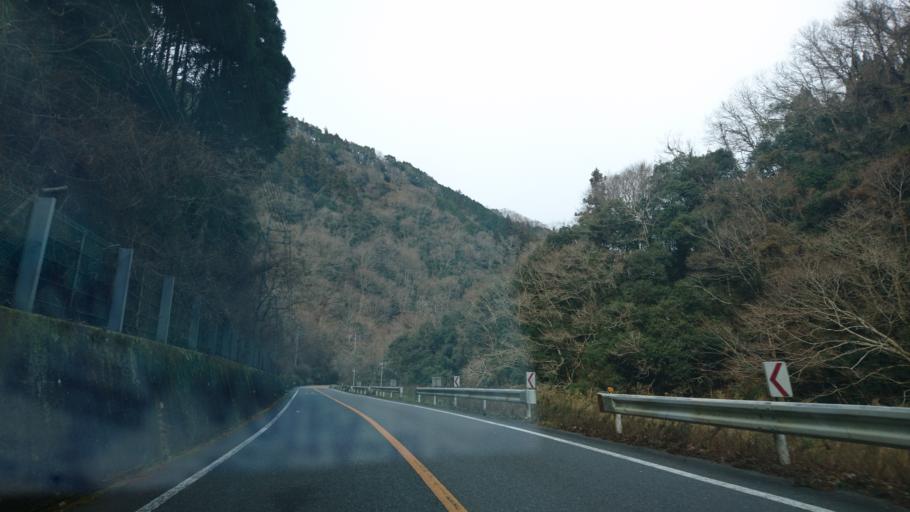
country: JP
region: Okayama
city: Takahashi
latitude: 34.8206
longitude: 133.6338
